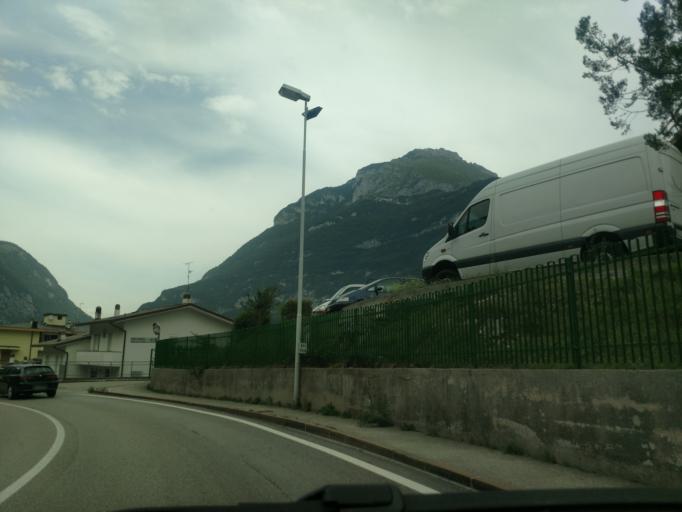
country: IT
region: Veneto
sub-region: Provincia di Belluno
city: Longarone
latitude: 46.2644
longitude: 12.3009
